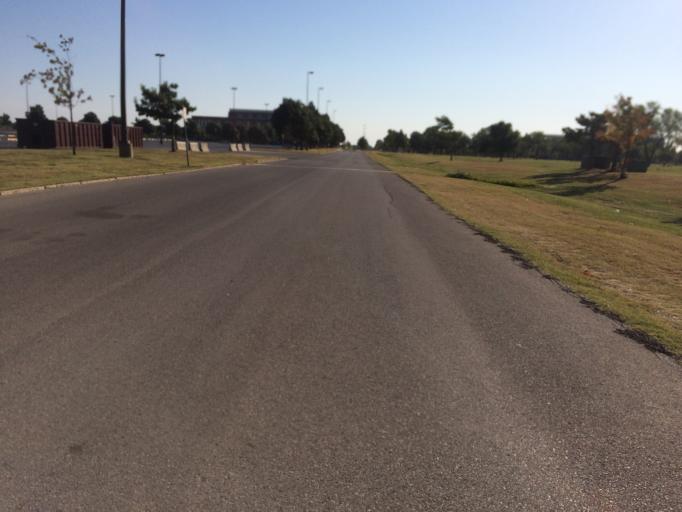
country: US
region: Oklahoma
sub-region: Cleveland County
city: Norman
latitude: 35.1852
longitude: -97.4452
